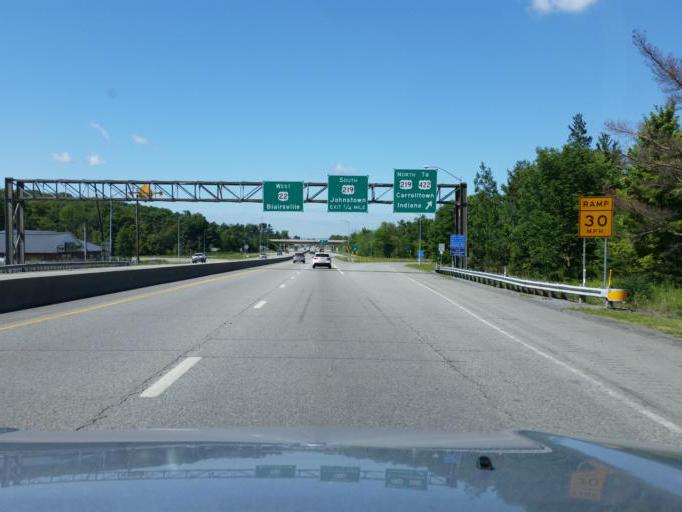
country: US
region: Pennsylvania
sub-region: Cambria County
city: Ebensburg
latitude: 40.4667
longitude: -78.7596
